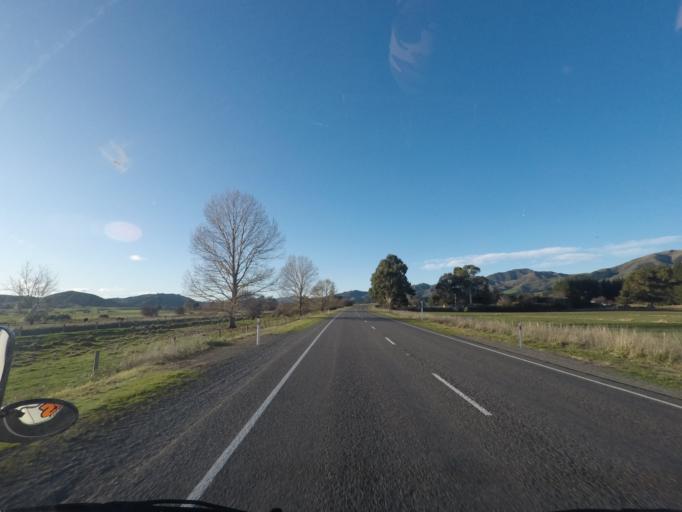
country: NZ
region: Canterbury
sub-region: Kaikoura District
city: Kaikoura
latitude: -42.7101
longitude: 173.2930
